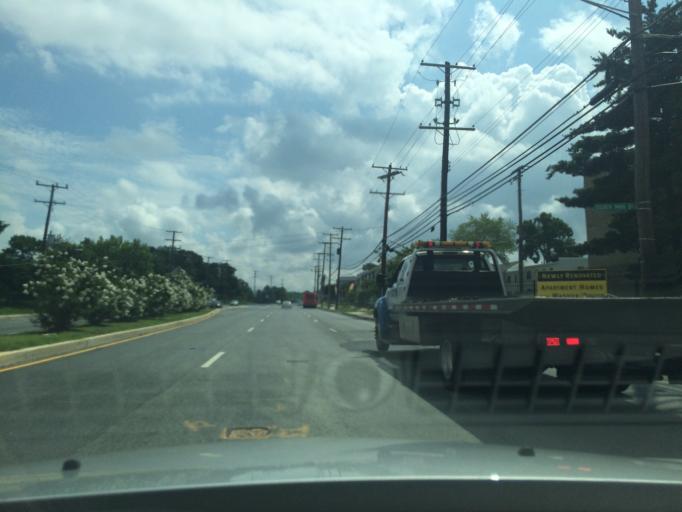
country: US
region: Maryland
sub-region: Prince George's County
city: Silver Hill
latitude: 38.8419
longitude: -76.9375
